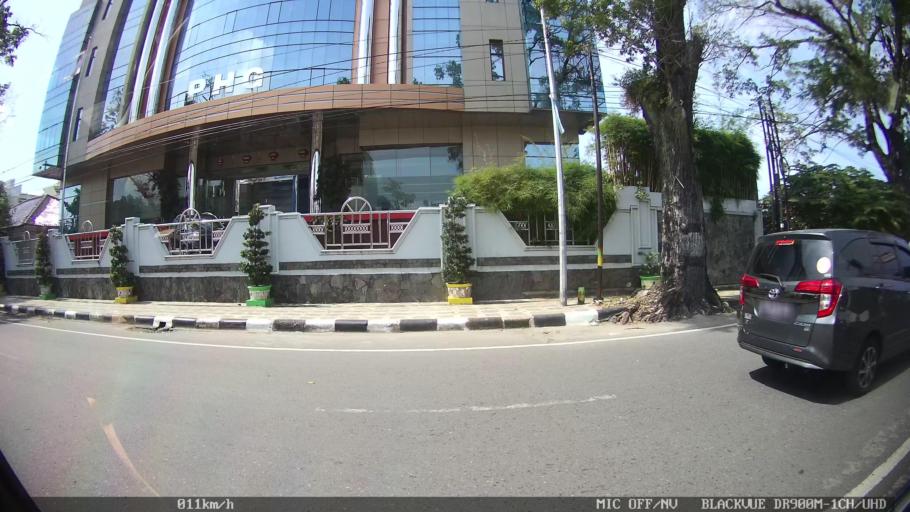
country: ID
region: North Sumatra
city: Medan
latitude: 3.5846
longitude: 98.6603
